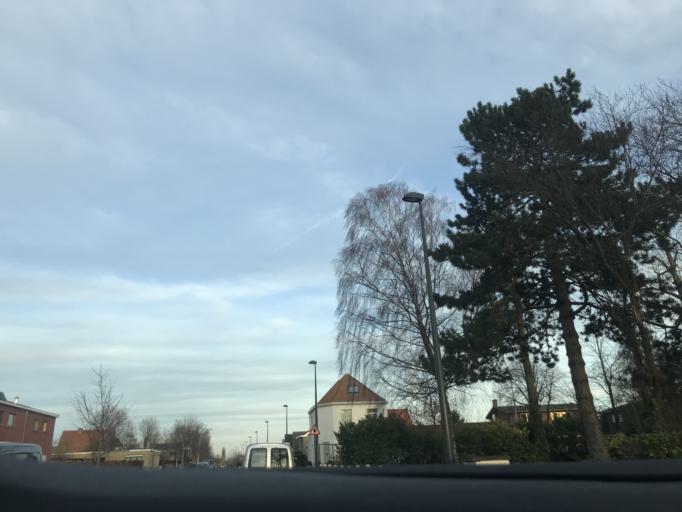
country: BE
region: Flanders
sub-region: Provincie Oost-Vlaanderen
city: Destelbergen
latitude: 51.0948
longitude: 3.7682
